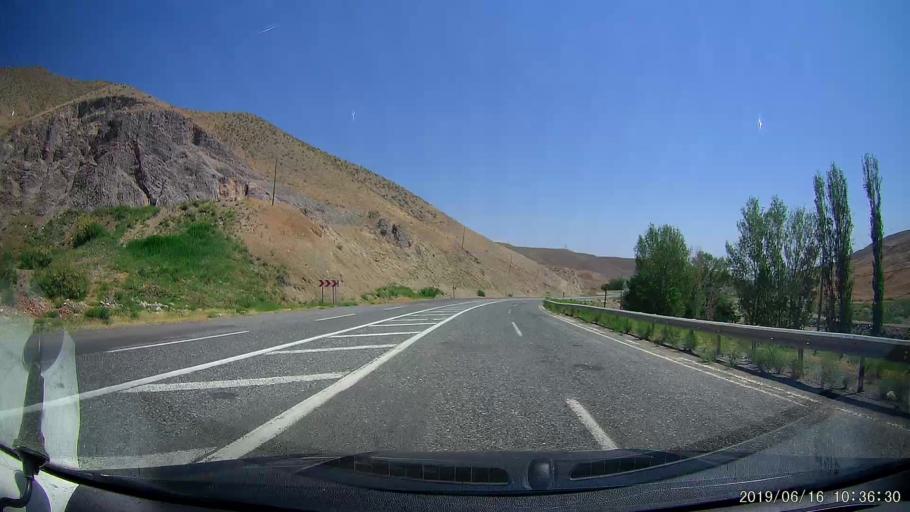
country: TR
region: Igdir
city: Tuzluca
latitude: 40.0388
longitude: 43.6819
